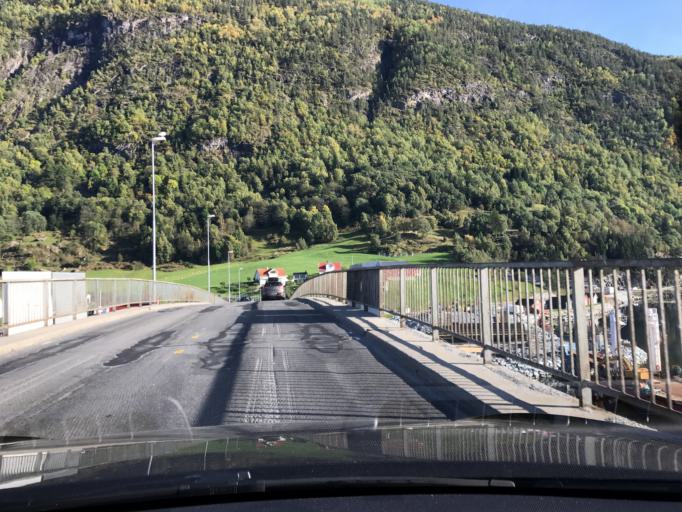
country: NO
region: Sogn og Fjordane
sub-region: Sogndal
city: Sogndalsfjora
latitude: 61.2313
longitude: 7.1202
